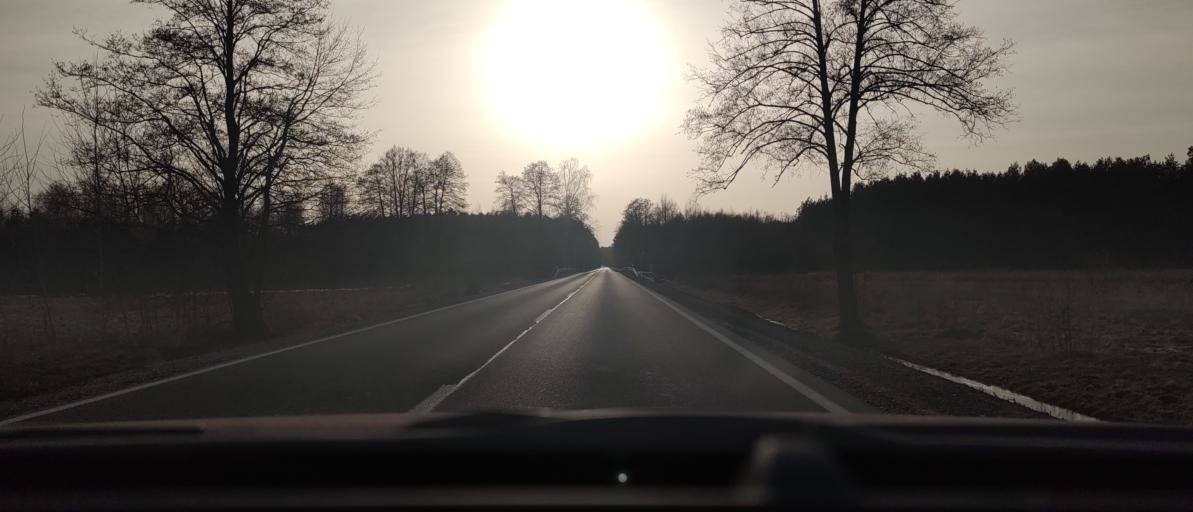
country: PL
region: Masovian Voivodeship
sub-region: Powiat bialobrzeski
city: Sucha
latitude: 51.6338
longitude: 20.8976
